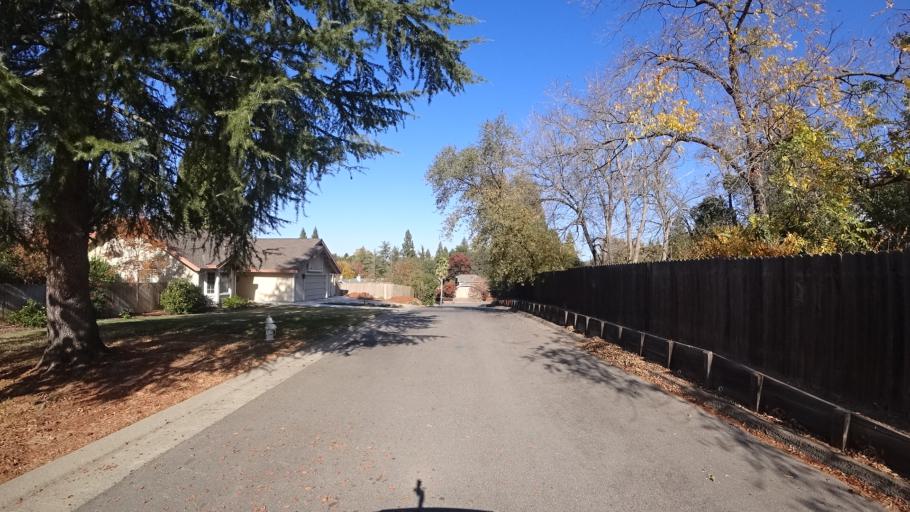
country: US
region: California
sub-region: Sacramento County
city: Citrus Heights
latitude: 38.6915
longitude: -121.2787
